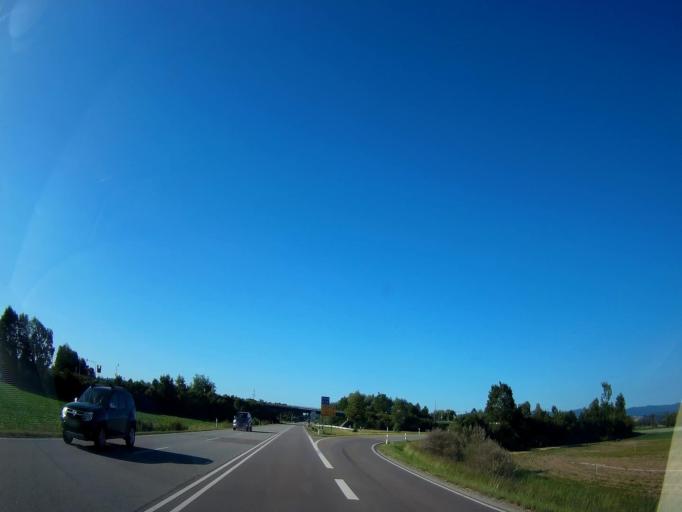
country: DE
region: Bavaria
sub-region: Lower Bavaria
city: Parkstetten
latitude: 48.9112
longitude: 12.6167
